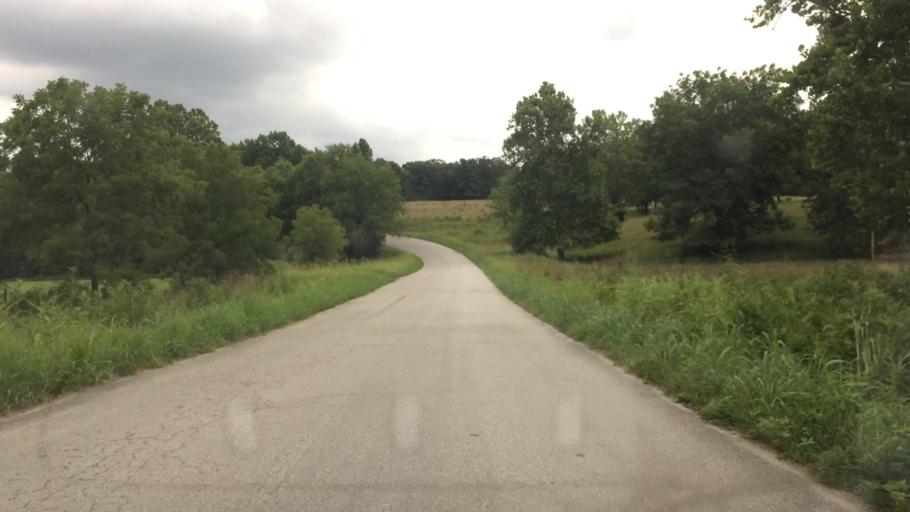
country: US
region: Missouri
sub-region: Greene County
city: Strafford
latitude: 37.3081
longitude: -93.0708
